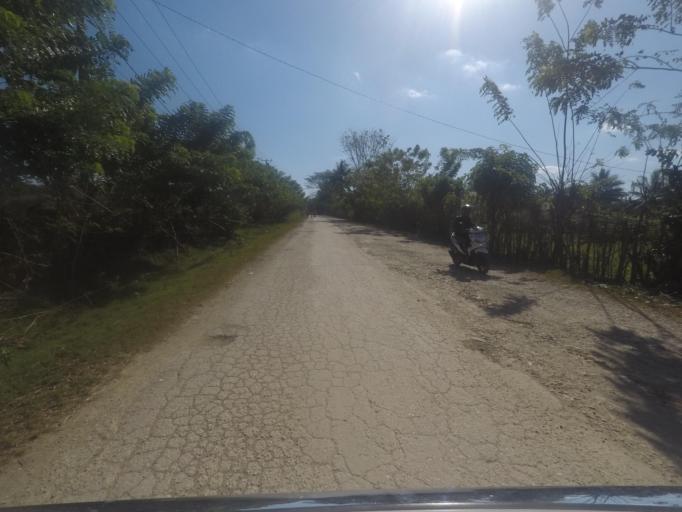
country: TL
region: Lautem
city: Lospalos
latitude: -8.5082
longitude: 126.9934
